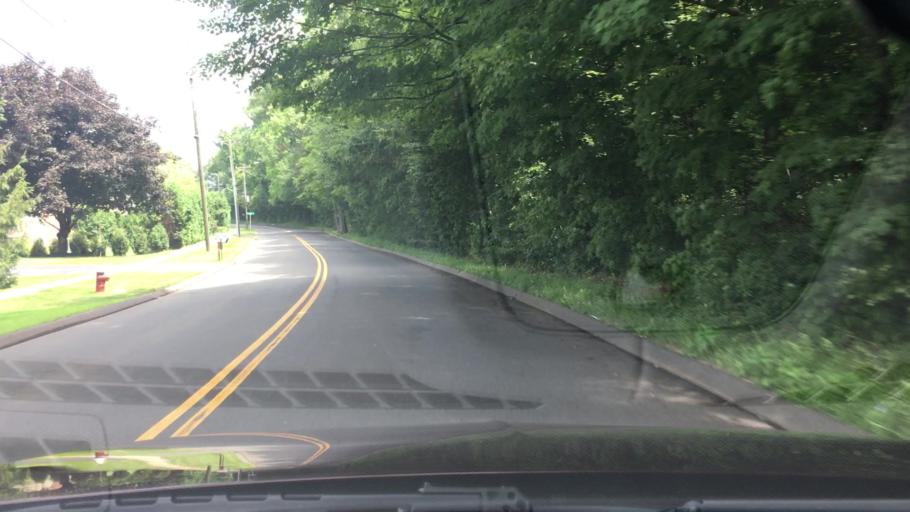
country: US
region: Connecticut
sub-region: Hartford County
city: Kensington
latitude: 41.6362
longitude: -72.7261
